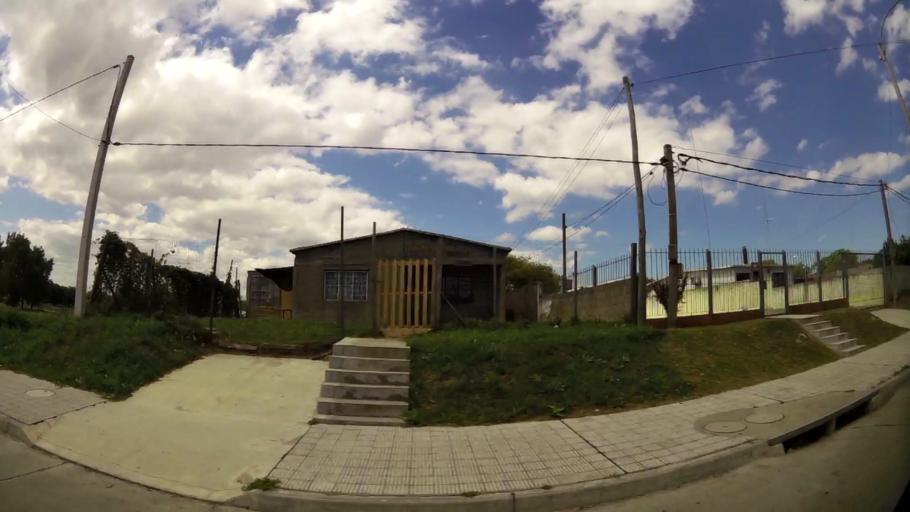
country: UY
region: Montevideo
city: Montevideo
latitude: -34.8422
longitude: -56.2445
